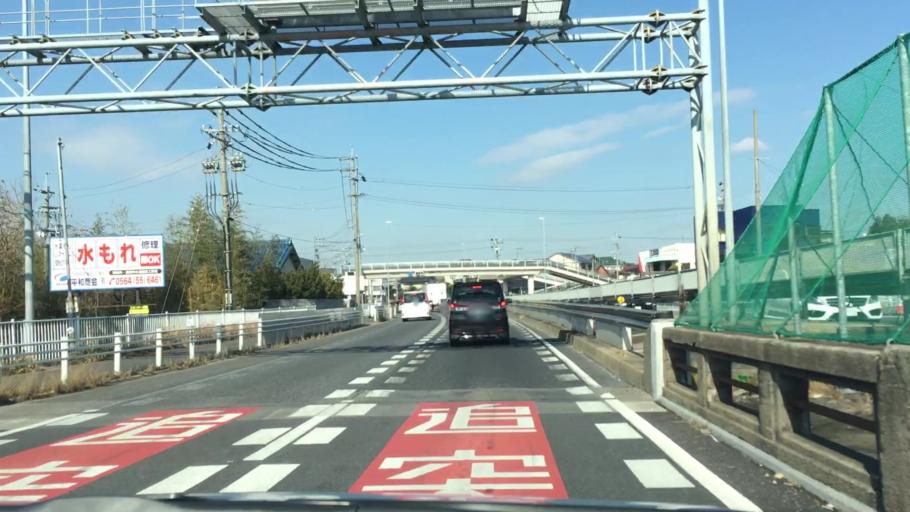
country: JP
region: Aichi
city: Okazaki
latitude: 34.9347
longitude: 137.1964
